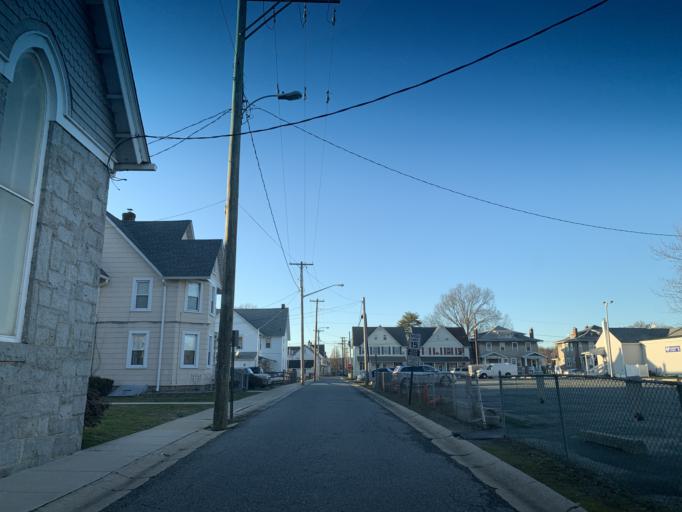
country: US
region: Maryland
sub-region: Cecil County
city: Perryville
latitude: 39.5586
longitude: -76.0751
